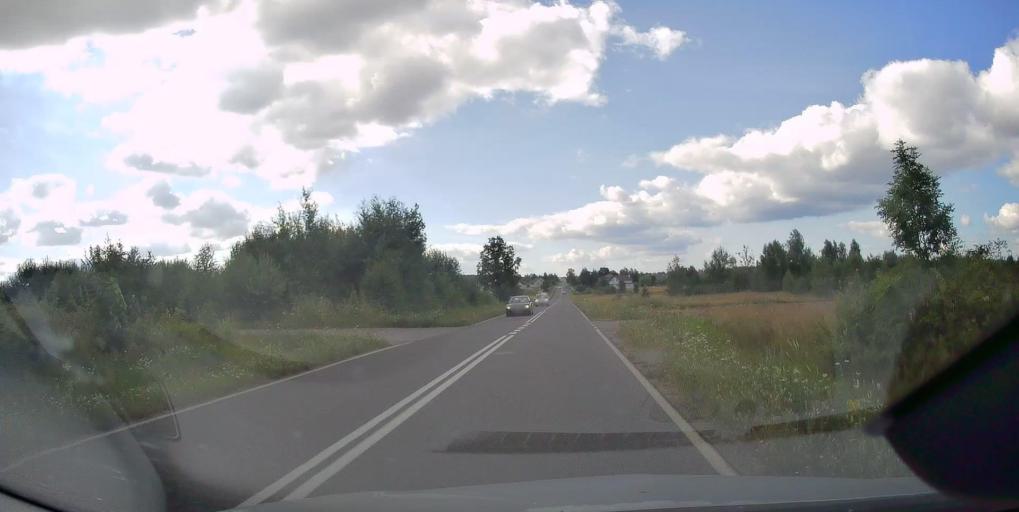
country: PL
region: Swietokrzyskie
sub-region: Powiat kielecki
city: Bodzentyn
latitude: 50.9070
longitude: 21.0082
